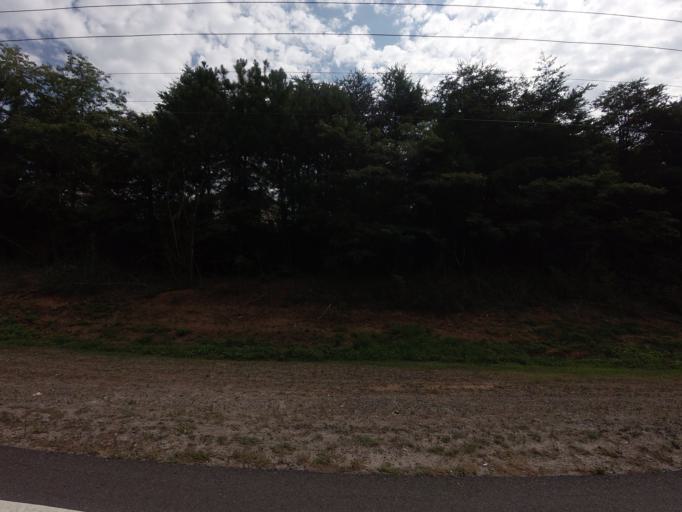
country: US
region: Georgia
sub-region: Fulton County
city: Johns Creek
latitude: 34.0338
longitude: -84.1704
